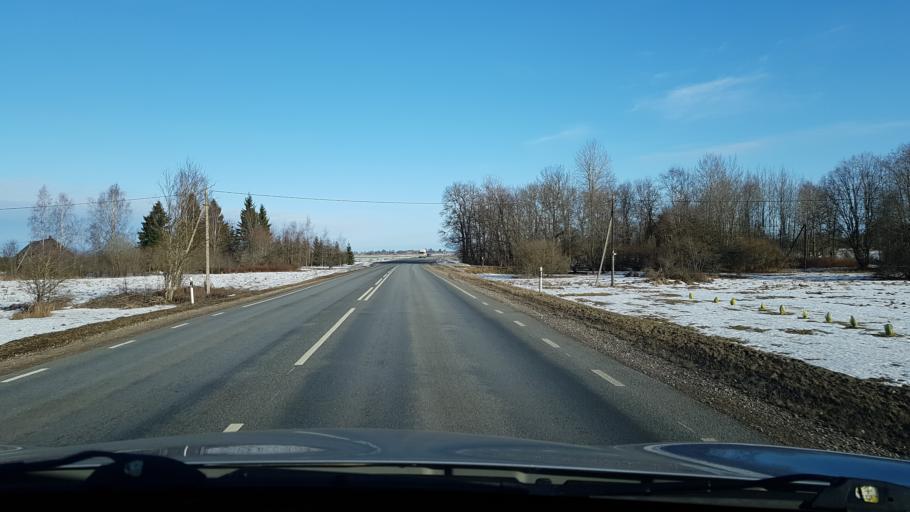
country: EE
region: Viljandimaa
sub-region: Vohma linn
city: Vohma
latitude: 58.6386
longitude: 25.5758
